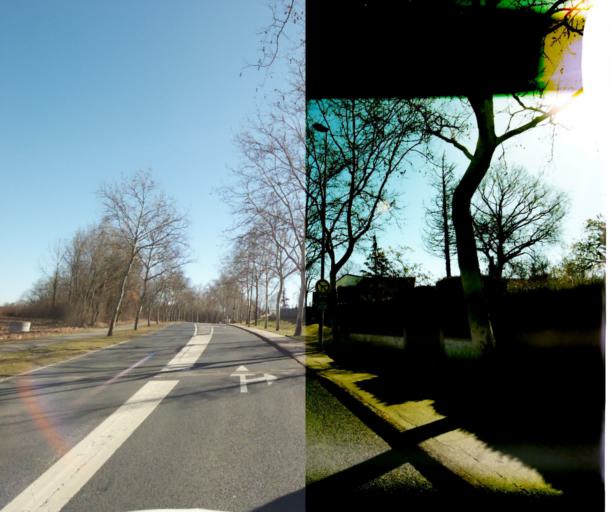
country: FR
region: Lorraine
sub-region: Departement de Meurthe-et-Moselle
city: Heillecourt
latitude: 48.6560
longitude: 6.1997
